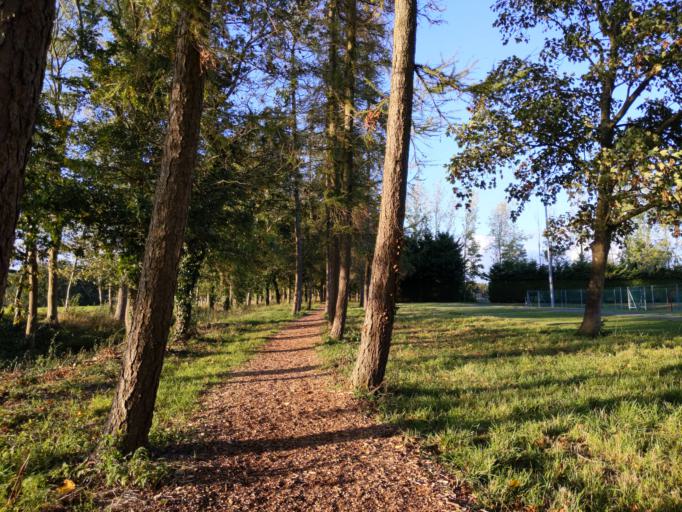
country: GB
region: England
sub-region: Oxfordshire
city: Radley
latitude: 51.6965
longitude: -1.2474
